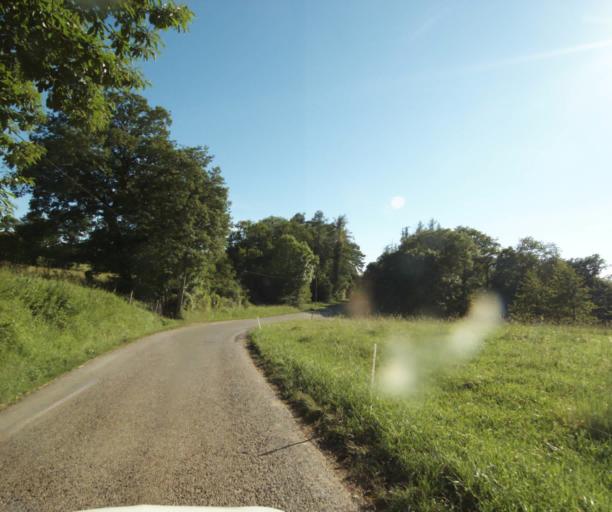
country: FR
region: Rhone-Alpes
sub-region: Departement de la Haute-Savoie
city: Ballaison
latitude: 46.3040
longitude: 6.3331
